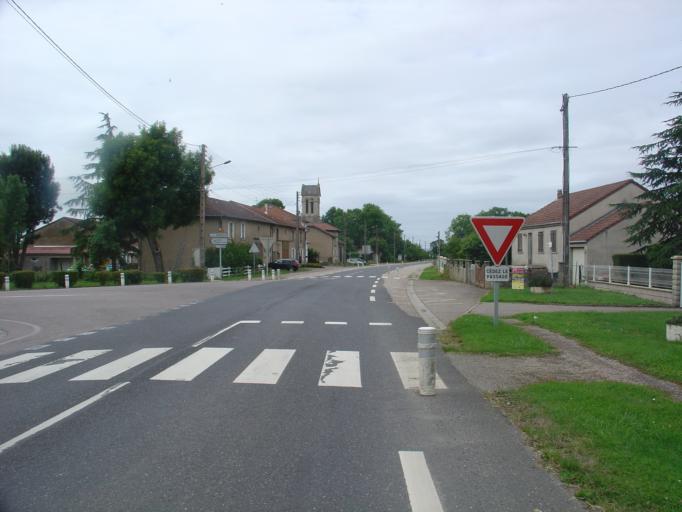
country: FR
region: Lorraine
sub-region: Departement de la Meuse
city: Vigneulles-les-Hattonchatel
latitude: 48.8525
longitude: 5.7893
